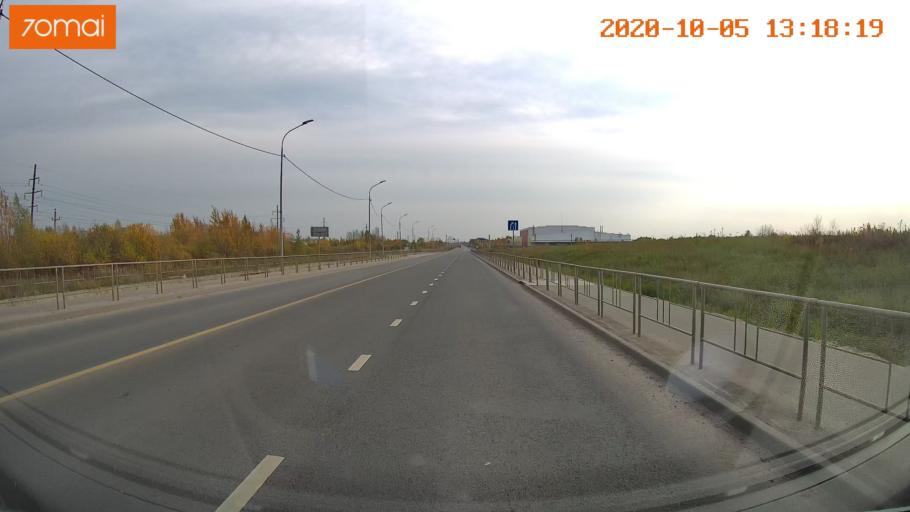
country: RU
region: Ivanovo
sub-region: Gorod Ivanovo
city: Ivanovo
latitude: 56.9782
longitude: 40.9190
